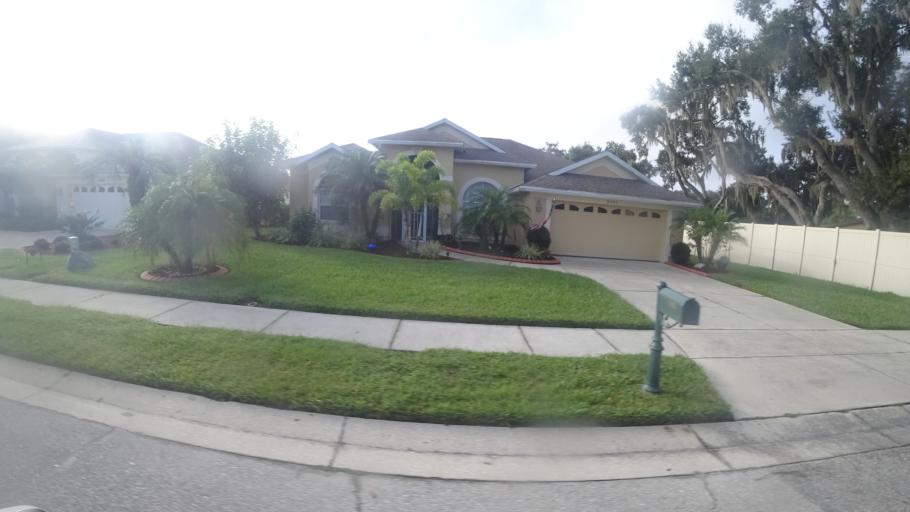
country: US
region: Florida
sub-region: Manatee County
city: Ellenton
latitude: 27.5391
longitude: -82.4785
